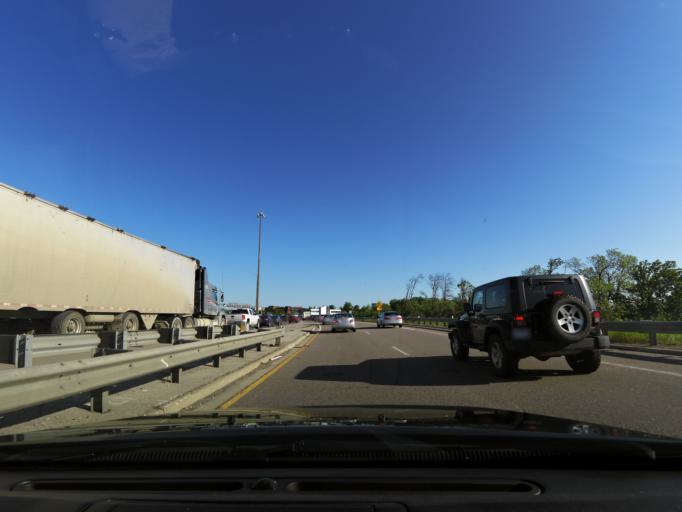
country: CA
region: Ontario
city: Waterloo
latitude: 43.4709
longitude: -80.4746
